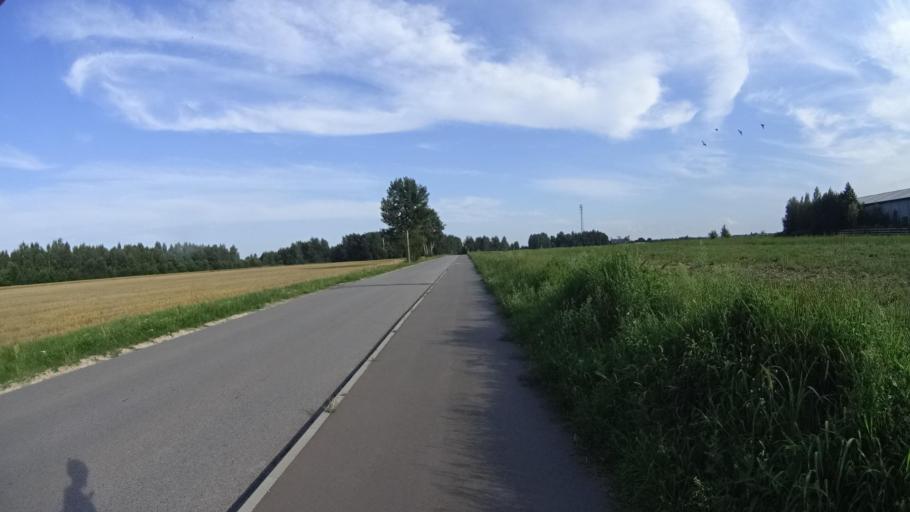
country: PL
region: Masovian Voivodeship
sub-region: Powiat piaseczynski
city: Tarczyn
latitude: 52.0221
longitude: 20.7873
